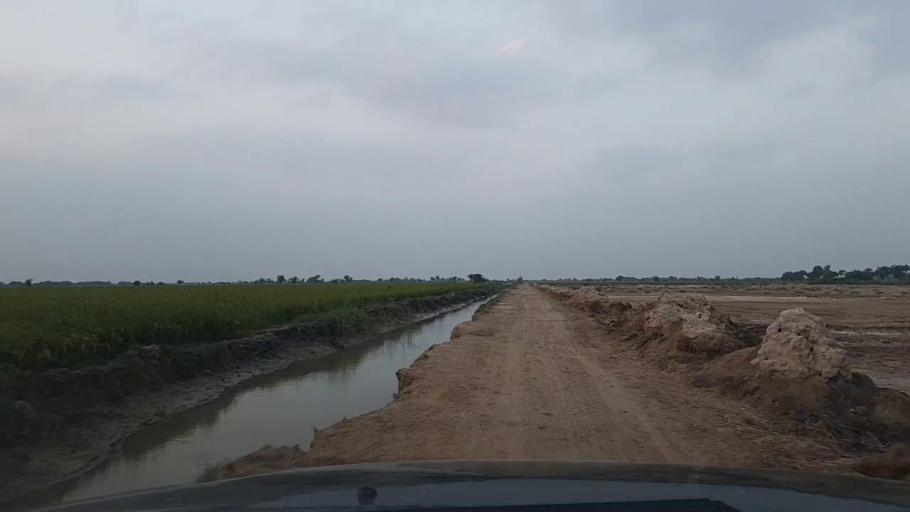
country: PK
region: Sindh
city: Jati
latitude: 24.5011
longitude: 68.3931
